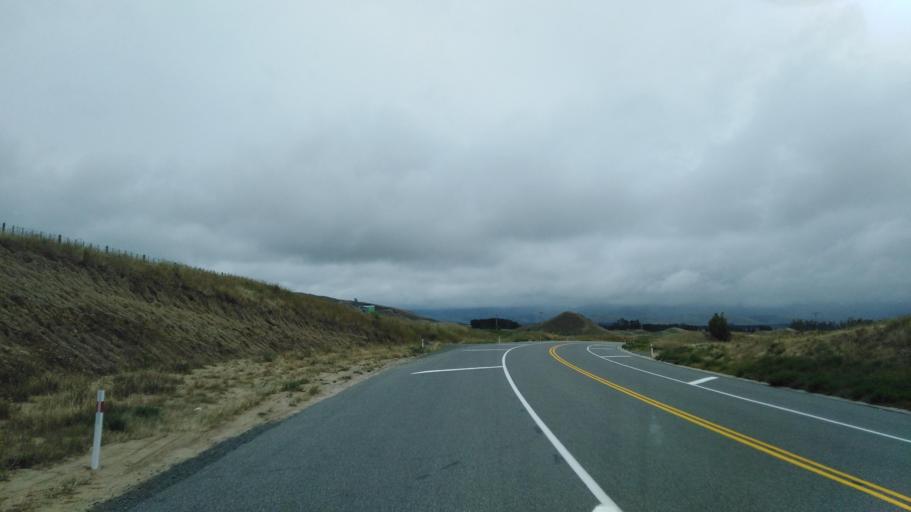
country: NZ
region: Marlborough
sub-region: Marlborough District
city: Blenheim
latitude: -41.6925
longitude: 174.0820
